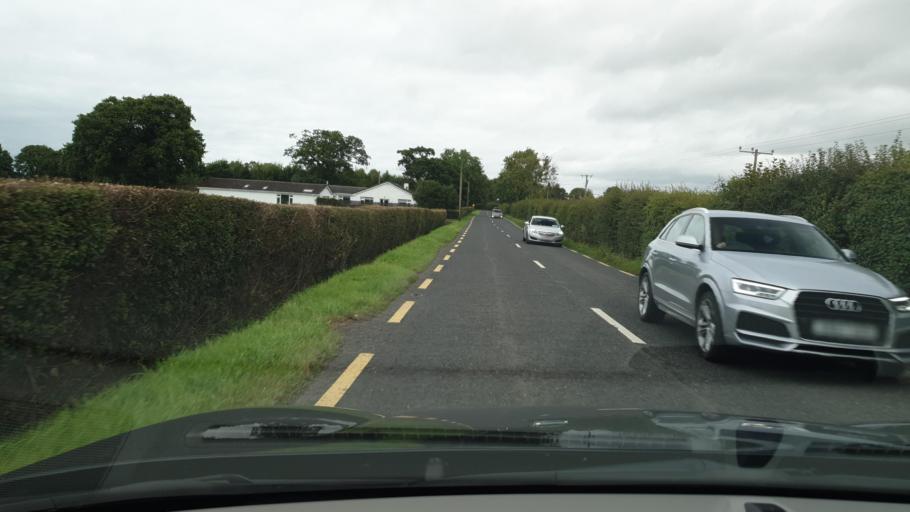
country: IE
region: Leinster
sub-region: Kildare
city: Maynooth
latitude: 53.3629
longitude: -6.6260
